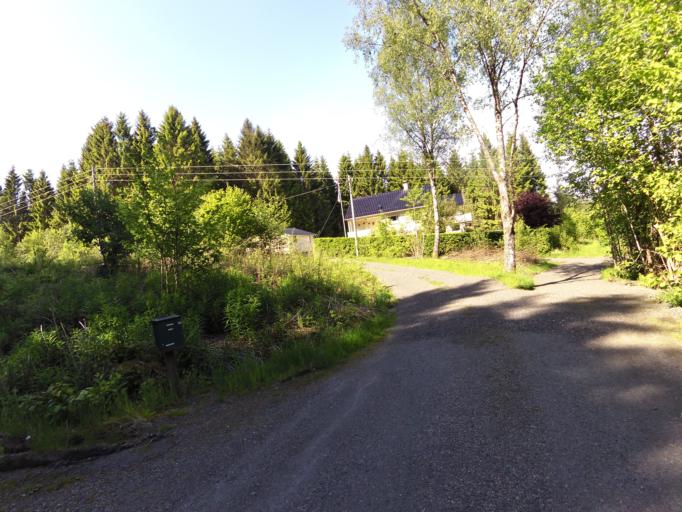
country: NO
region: Hordaland
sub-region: Stord
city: Leirvik
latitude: 59.7867
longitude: 5.4792
